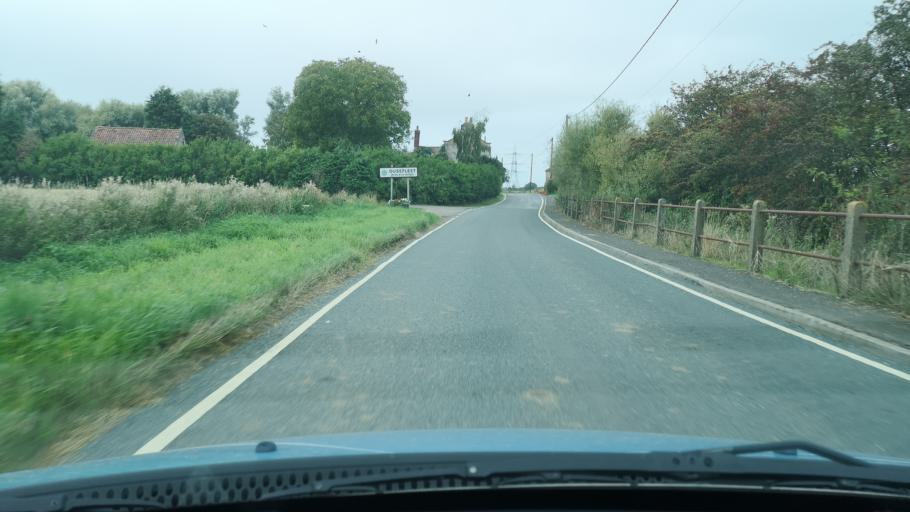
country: GB
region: England
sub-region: East Riding of Yorkshire
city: Laxton
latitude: 53.6978
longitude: -0.7359
